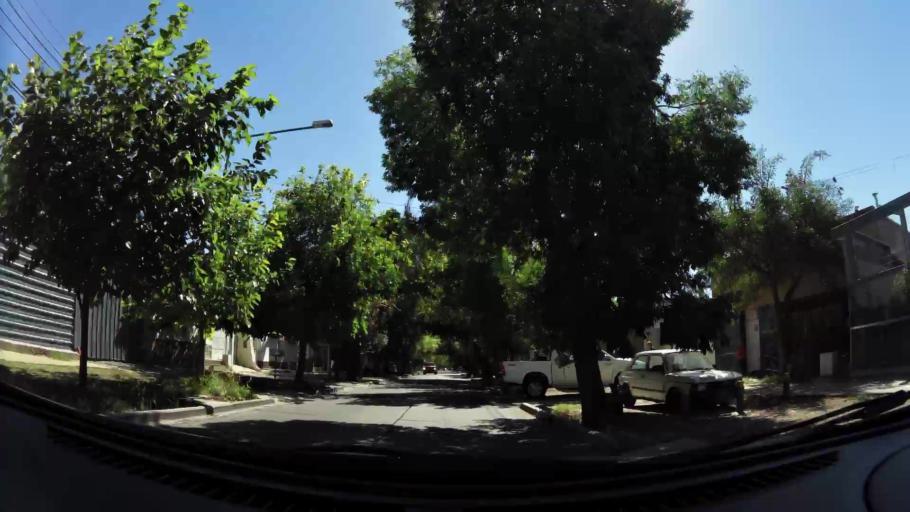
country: AR
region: Mendoza
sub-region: Departamento de Godoy Cruz
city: Godoy Cruz
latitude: -32.9504
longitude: -68.8410
